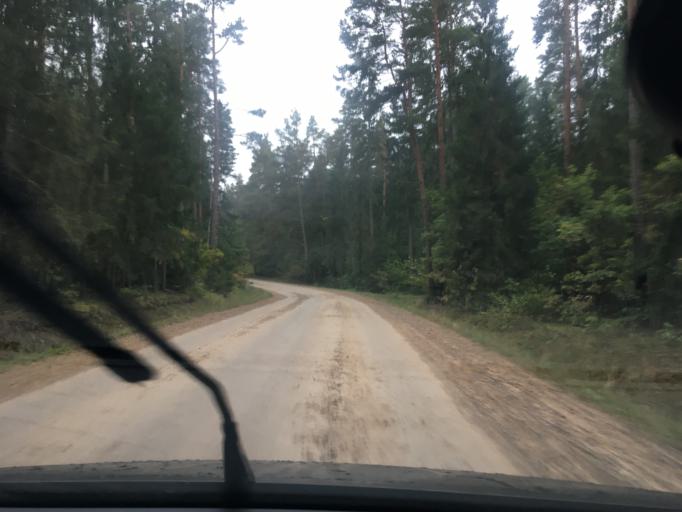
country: LV
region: Kuldigas Rajons
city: Kuldiga
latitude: 56.9918
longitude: 21.9744
